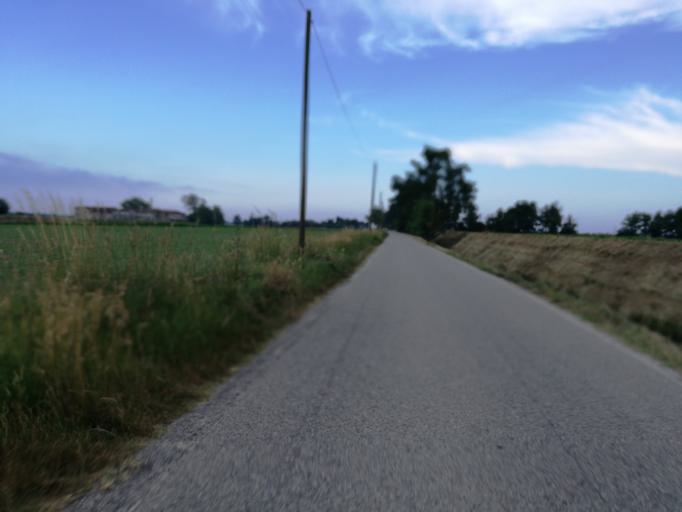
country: IT
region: Piedmont
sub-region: Provincia di Novara
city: Torrion Quartara
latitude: 45.3958
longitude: 8.6196
